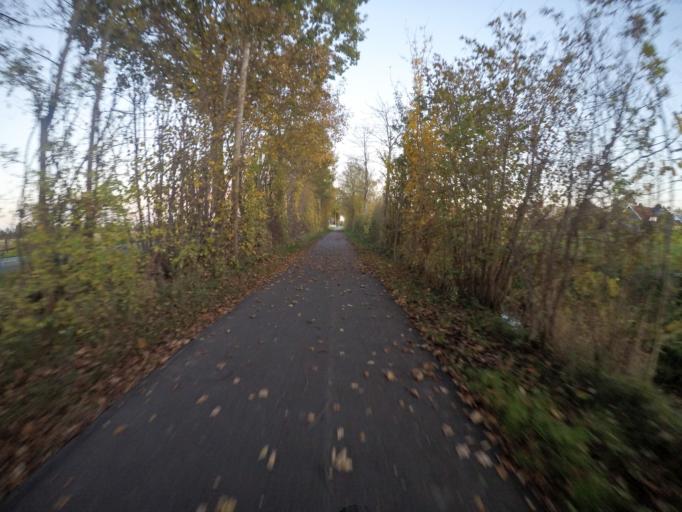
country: DE
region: North Rhine-Westphalia
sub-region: Regierungsbezirk Munster
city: Isselburg
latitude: 51.8422
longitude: 6.5237
